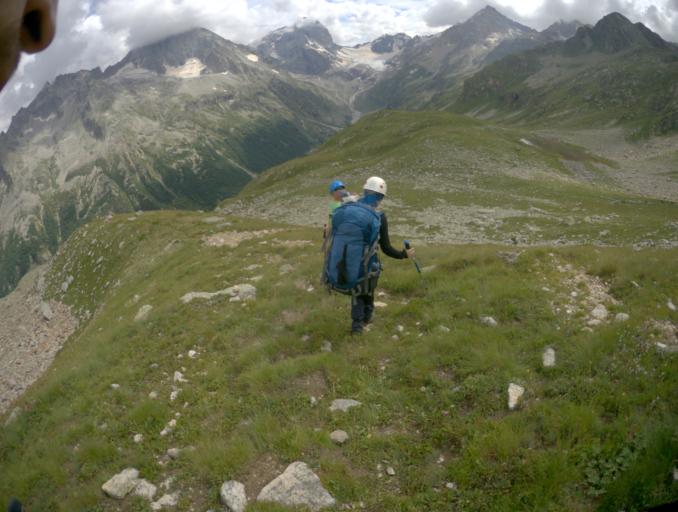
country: RU
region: Karachayevo-Cherkesiya
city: Uchkulan
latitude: 43.2706
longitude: 42.1264
